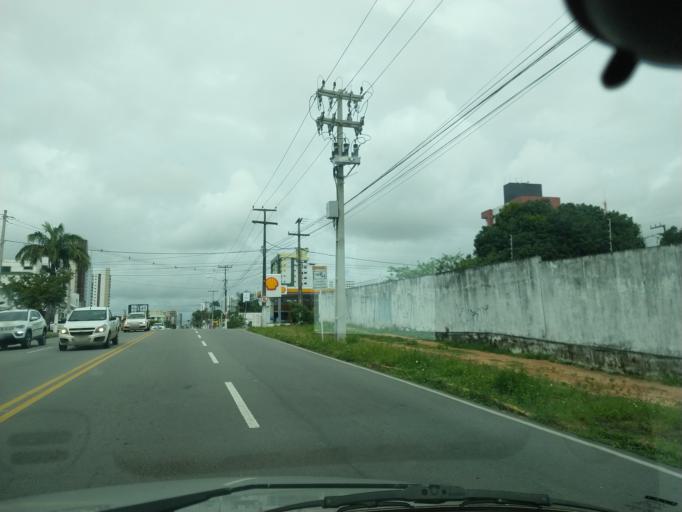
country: BR
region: Rio Grande do Norte
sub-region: Natal
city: Natal
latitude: -5.8155
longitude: -35.2172
